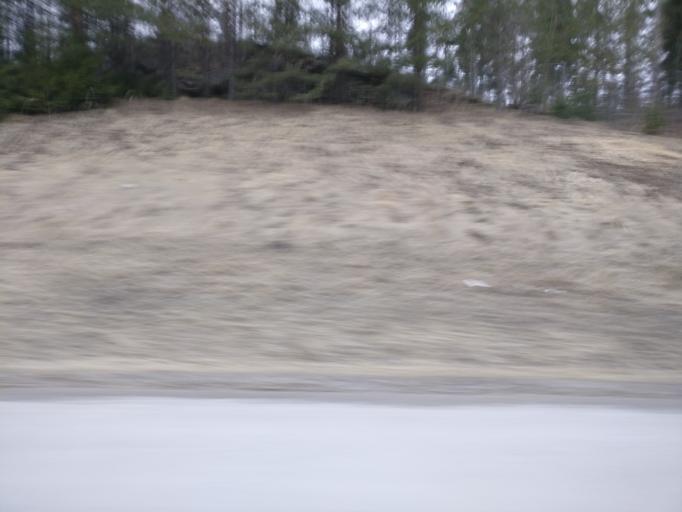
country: FI
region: Uusimaa
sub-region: Helsinki
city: Nurmijaervi
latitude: 60.3747
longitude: 24.8131
